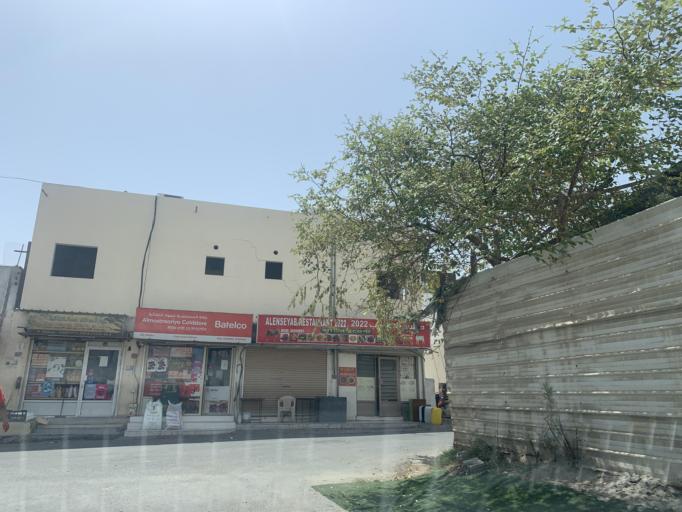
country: BH
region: Central Governorate
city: Madinat Hamad
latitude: 26.1513
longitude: 50.4982
